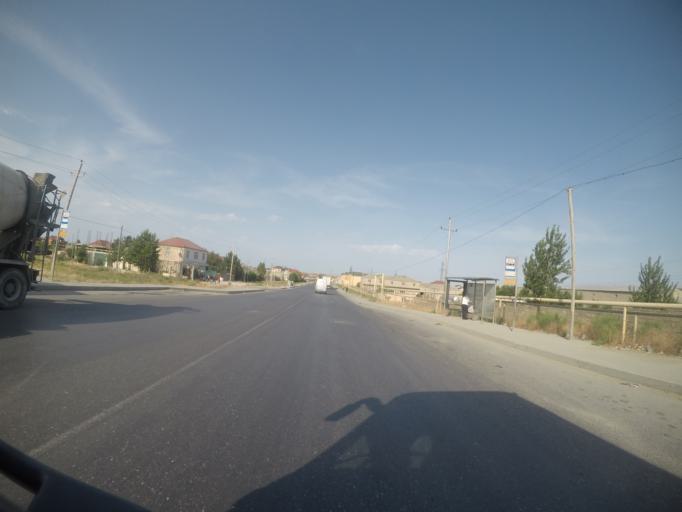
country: AZ
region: Baki
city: Bilajari
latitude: 40.4452
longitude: 49.7937
